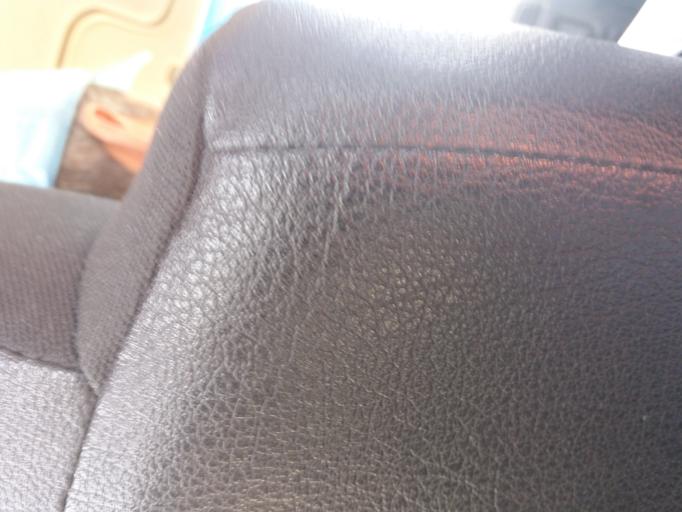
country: MX
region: Aguascalientes
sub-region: Aguascalientes
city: San Sebastian [Fraccionamiento]
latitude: 21.8122
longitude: -102.3065
